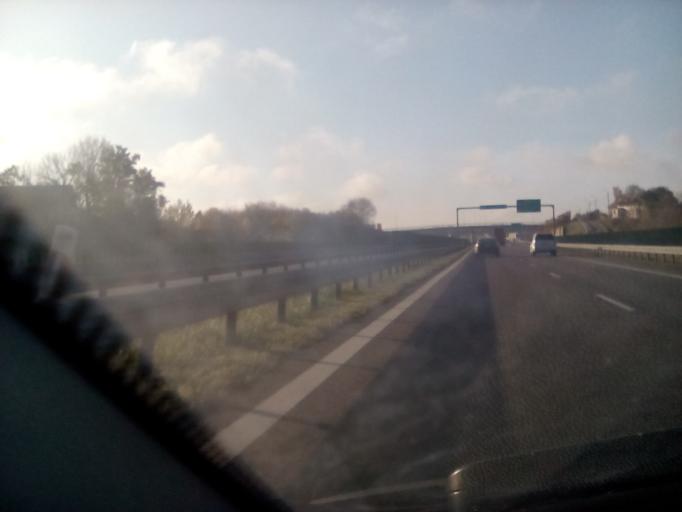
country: PL
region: Masovian Voivodeship
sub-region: Powiat grojecki
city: Grojec
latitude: 51.8748
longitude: 20.8542
